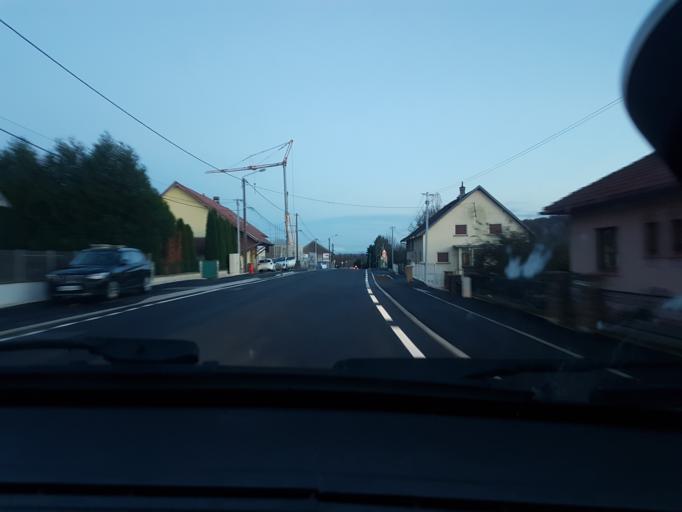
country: FR
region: Franche-Comte
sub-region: Territoire de Belfort
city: Essert
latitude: 47.6364
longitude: 6.8065
